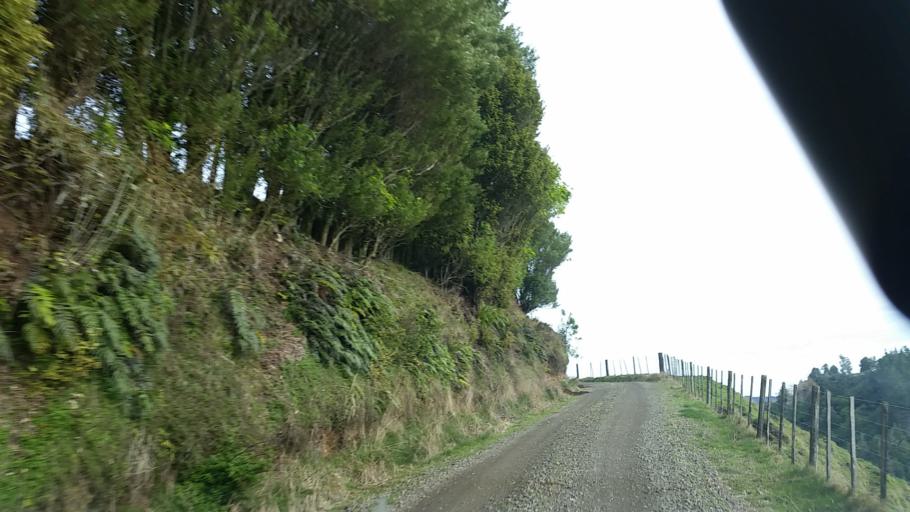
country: NZ
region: Taranaki
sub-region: New Plymouth District
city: Waitara
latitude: -39.0720
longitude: 174.4008
